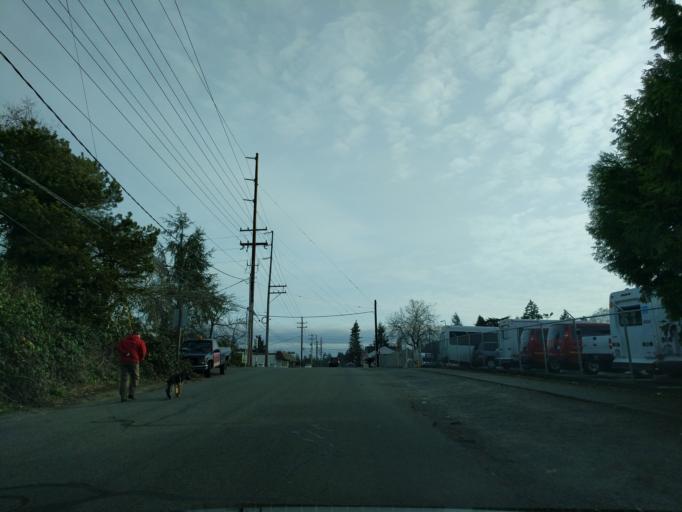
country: US
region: Washington
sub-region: King County
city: Shoreline
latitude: 47.7487
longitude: -122.3254
